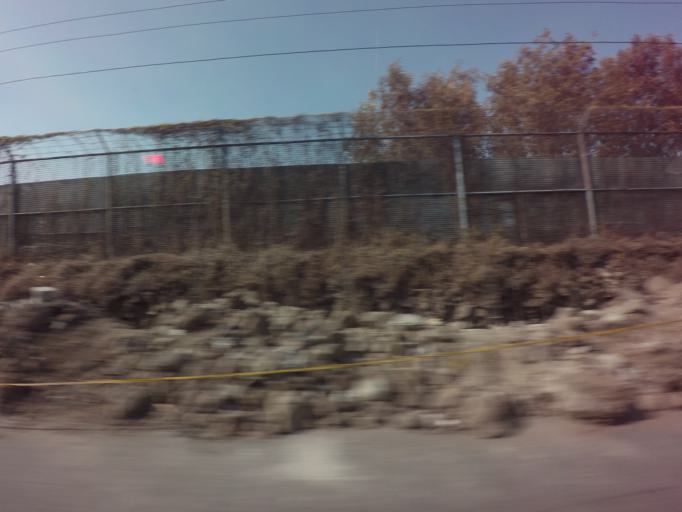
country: PH
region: Calabarzon
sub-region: Province of Rizal
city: Taguig
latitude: 14.5006
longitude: 121.0461
